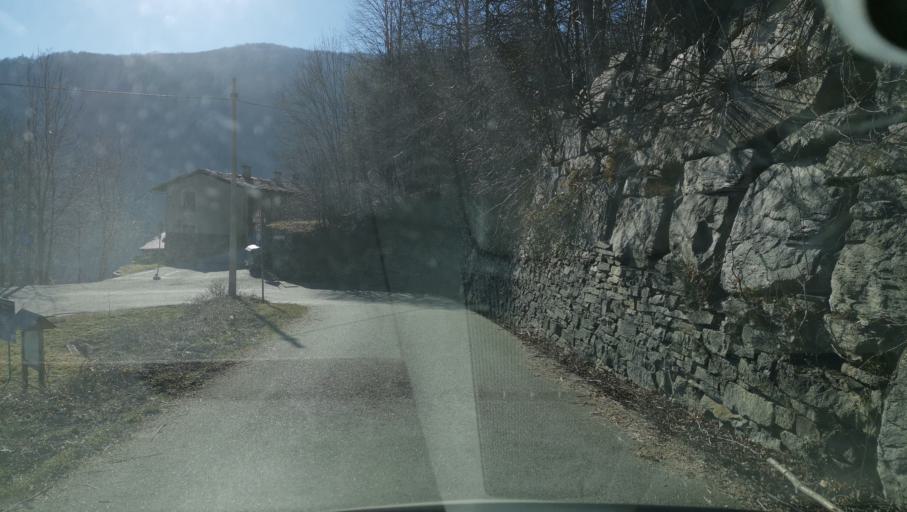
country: IT
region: Piedmont
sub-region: Provincia di Torino
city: Rora
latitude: 44.7906
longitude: 7.1946
